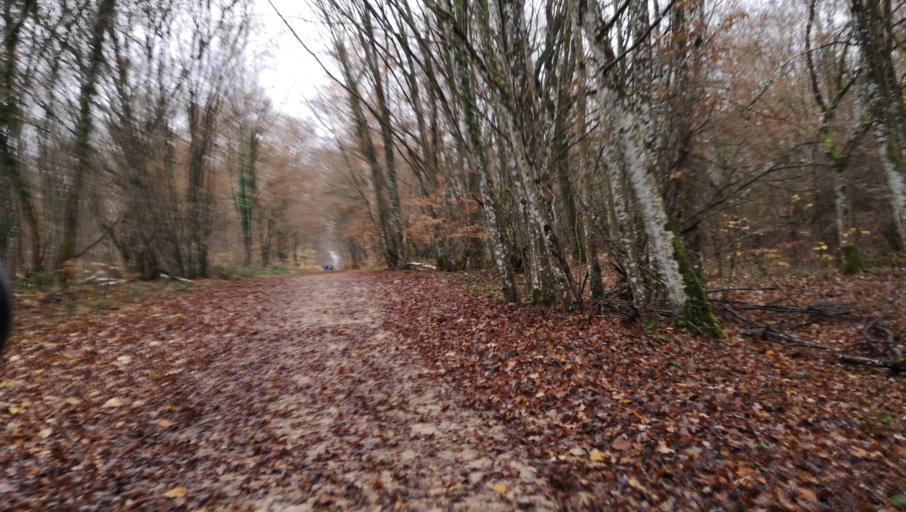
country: FR
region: Centre
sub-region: Departement du Loiret
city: Marigny-les-Usages
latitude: 47.9437
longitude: 1.9903
